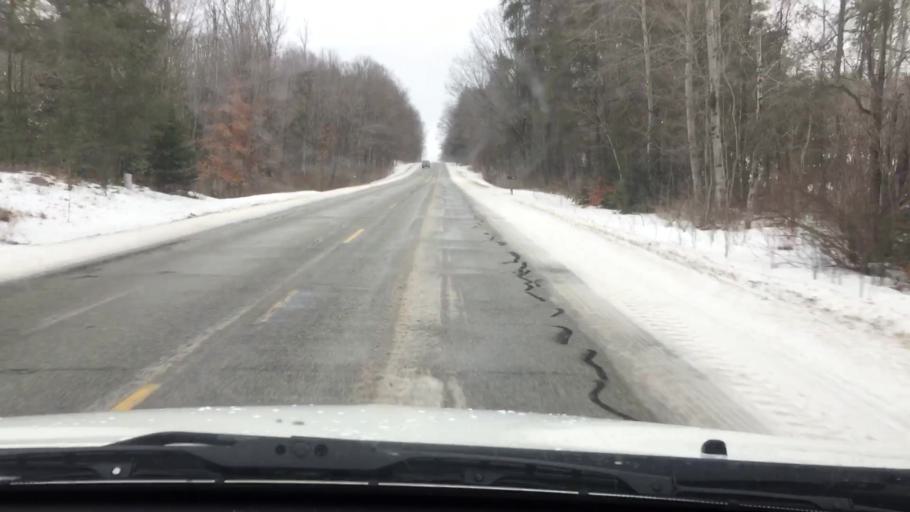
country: US
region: Michigan
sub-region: Wexford County
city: Cadillac
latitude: 44.1865
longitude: -85.4056
